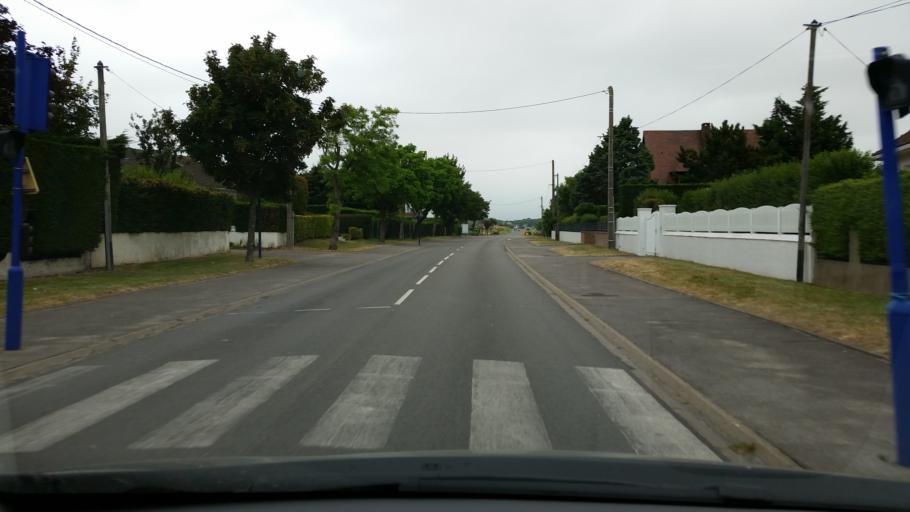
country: FR
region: Nord-Pas-de-Calais
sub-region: Departement du Pas-de-Calais
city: Marck
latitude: 50.9525
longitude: 1.9398
